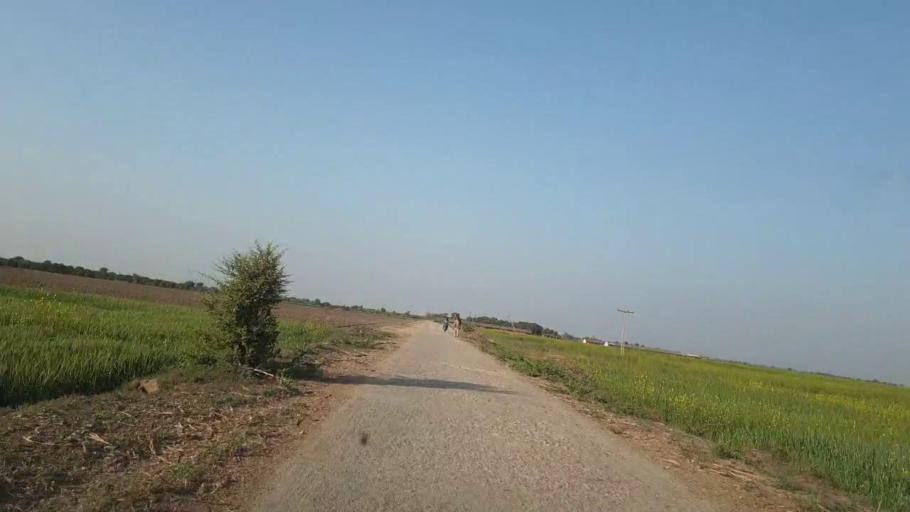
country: PK
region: Sindh
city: Tando Mittha Khan
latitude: 25.7452
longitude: 69.2397
